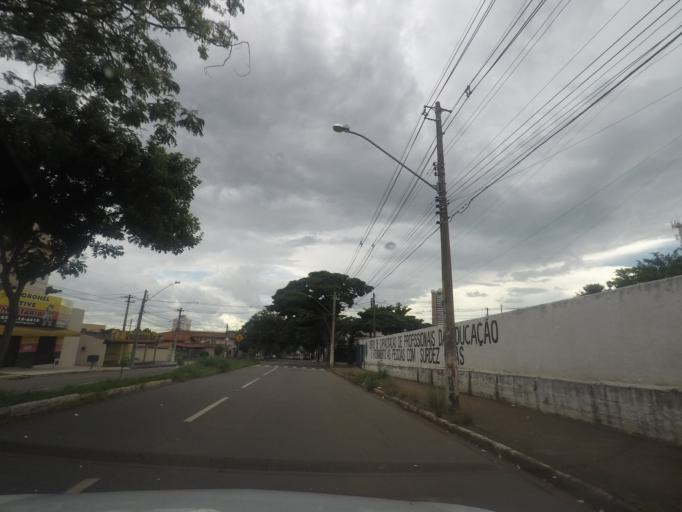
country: BR
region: Goias
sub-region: Goiania
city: Goiania
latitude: -16.6861
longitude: -49.2387
